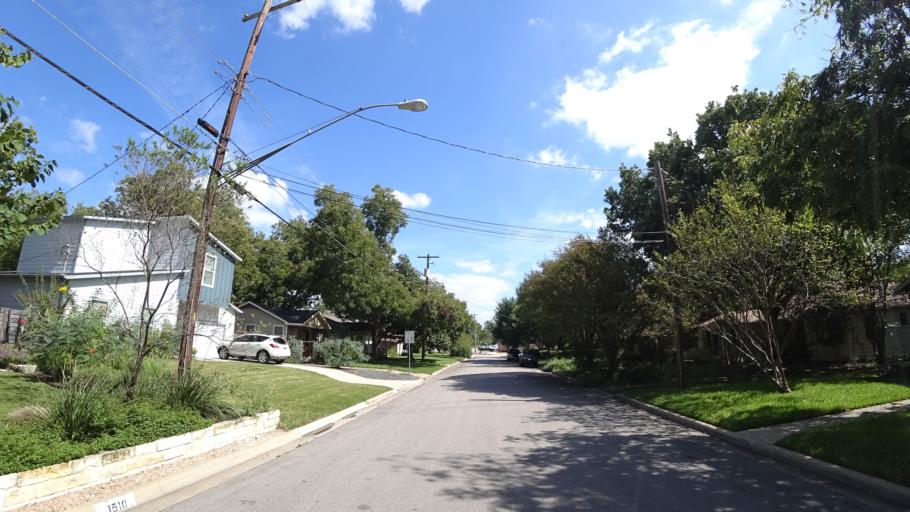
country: US
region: Texas
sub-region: Travis County
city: Austin
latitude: 30.3439
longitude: -97.7267
